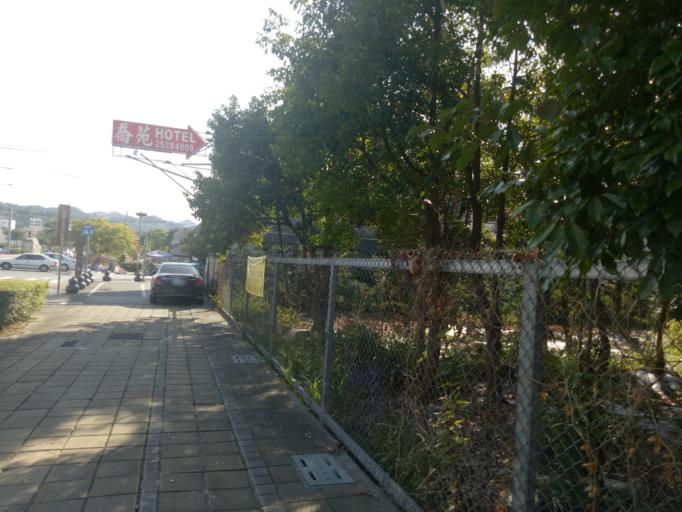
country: TW
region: Taiwan
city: Fengyuan
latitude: 24.2562
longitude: 120.7370
